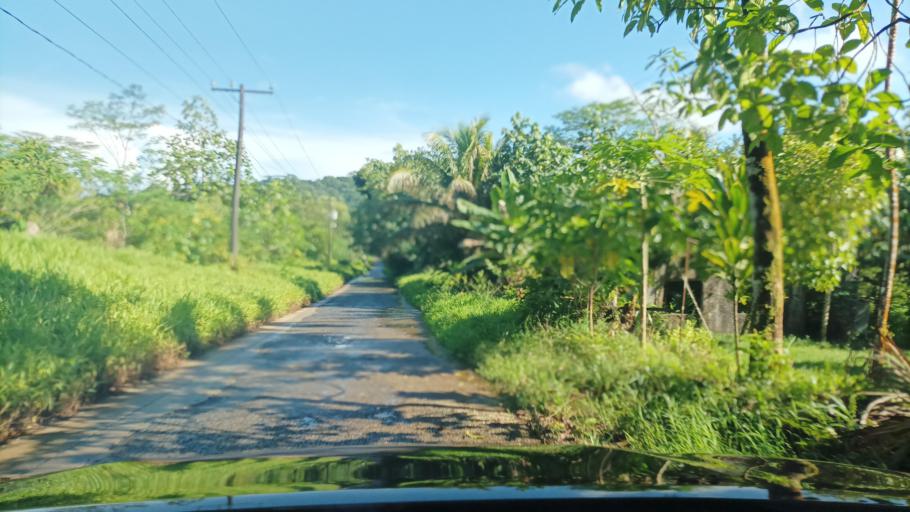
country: FM
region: Pohnpei
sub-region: Sokehs Municipality
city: Palikir - National Government Center
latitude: 6.9181
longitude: 158.1575
